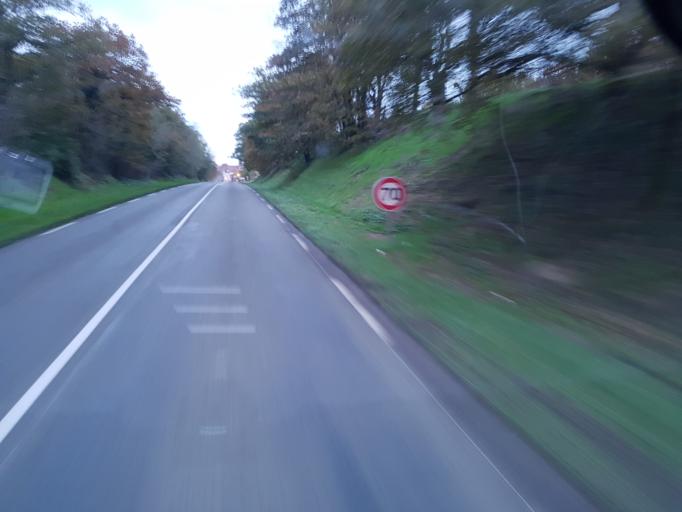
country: FR
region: Picardie
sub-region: Departement de l'Aisne
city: Coincy
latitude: 49.1449
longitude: 3.3872
